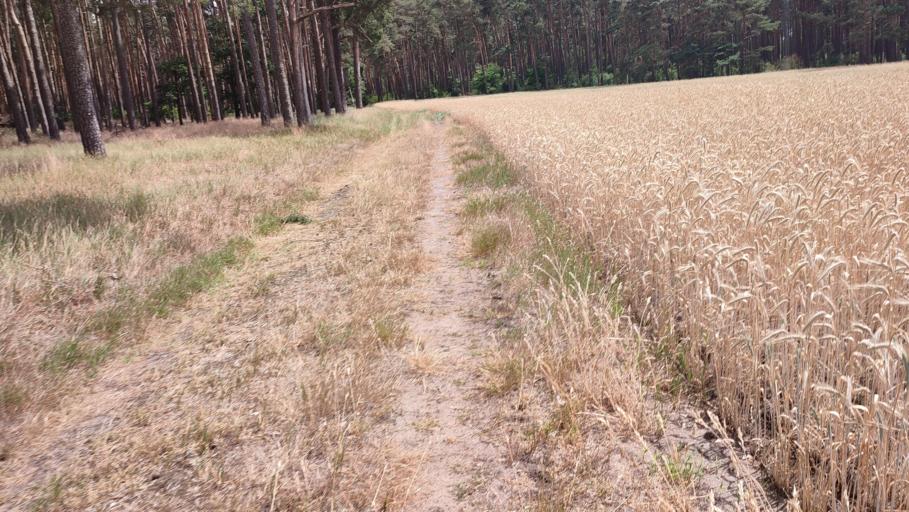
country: DE
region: Lower Saxony
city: Hitzacker
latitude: 53.2128
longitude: 11.0674
